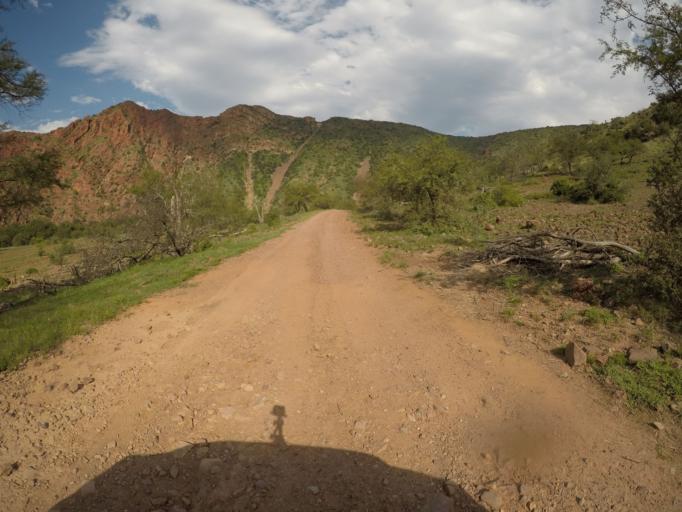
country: ZA
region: Eastern Cape
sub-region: Cacadu District Municipality
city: Kareedouw
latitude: -33.6401
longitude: 24.3170
